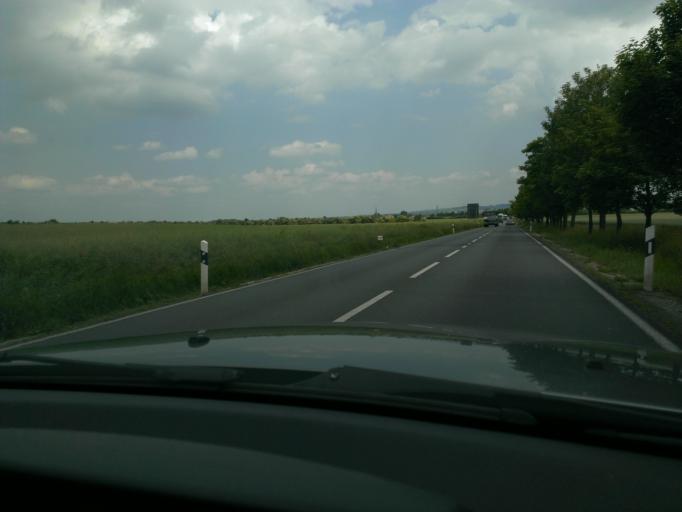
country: DE
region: Thuringia
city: Erfurt
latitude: 50.9979
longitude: 11.0782
